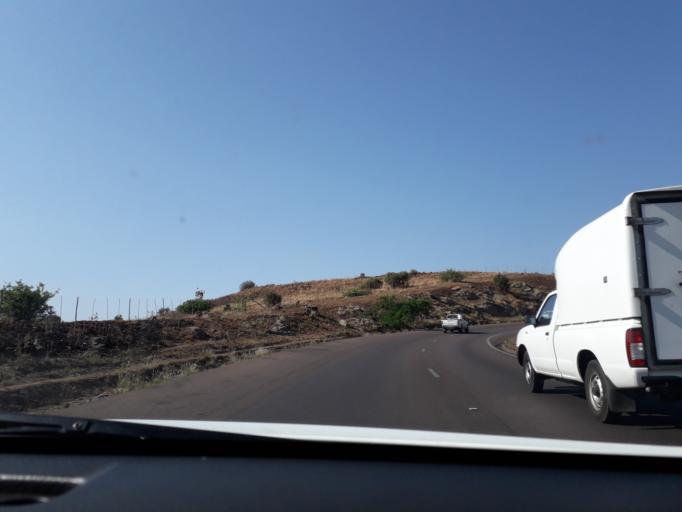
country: ZA
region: Gauteng
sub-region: City of Tshwane Metropolitan Municipality
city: Pretoria
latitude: -25.7845
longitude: 28.1924
